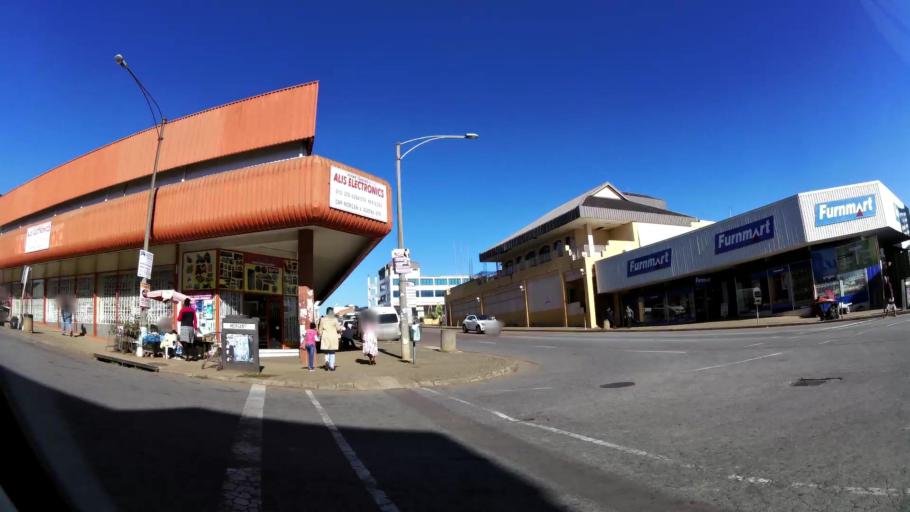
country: ZA
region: Limpopo
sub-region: Mopani District Municipality
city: Tzaneen
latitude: -23.8260
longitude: 30.1605
